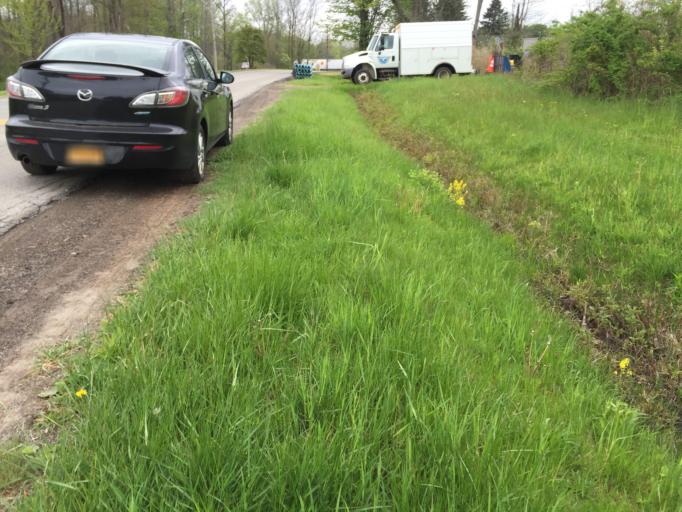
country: US
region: New York
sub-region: Wayne County
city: Marion
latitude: 43.1428
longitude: -77.1697
